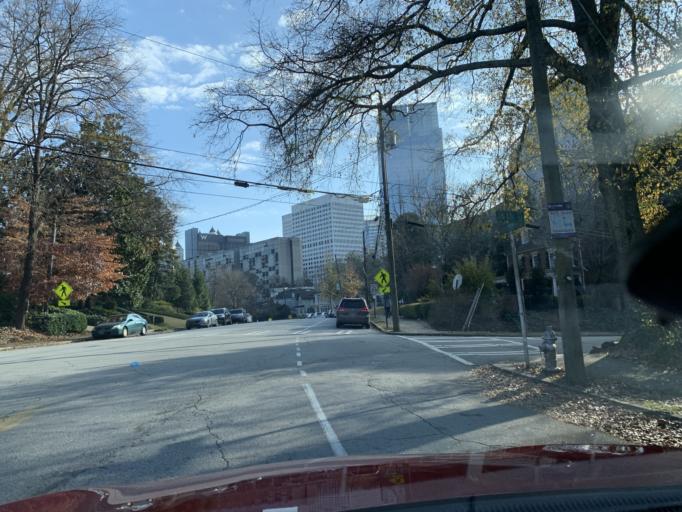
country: US
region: Georgia
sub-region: Fulton County
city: Atlanta
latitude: 33.7917
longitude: -84.3834
